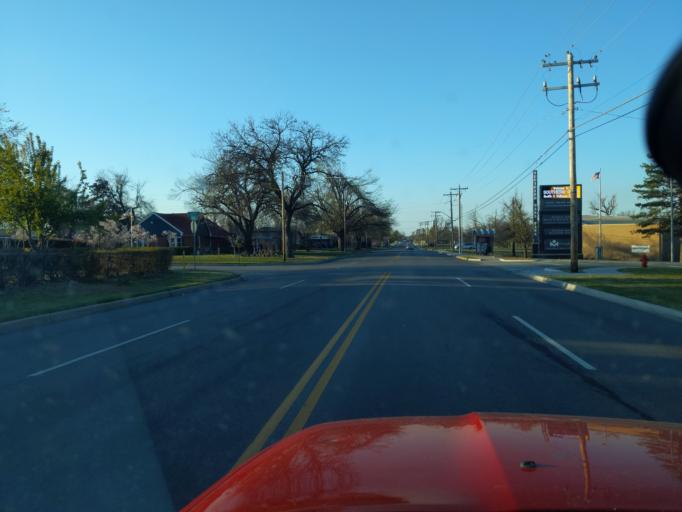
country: US
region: Oklahoma
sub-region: Cleveland County
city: Moore
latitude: 35.3963
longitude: -97.5218
